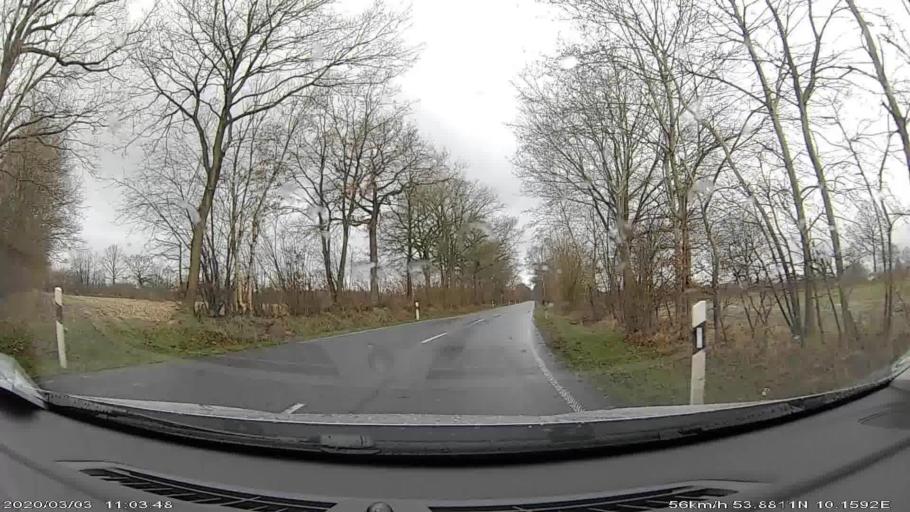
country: DE
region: Schleswig-Holstein
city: Stuvenborn
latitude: 53.8791
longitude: 10.1540
